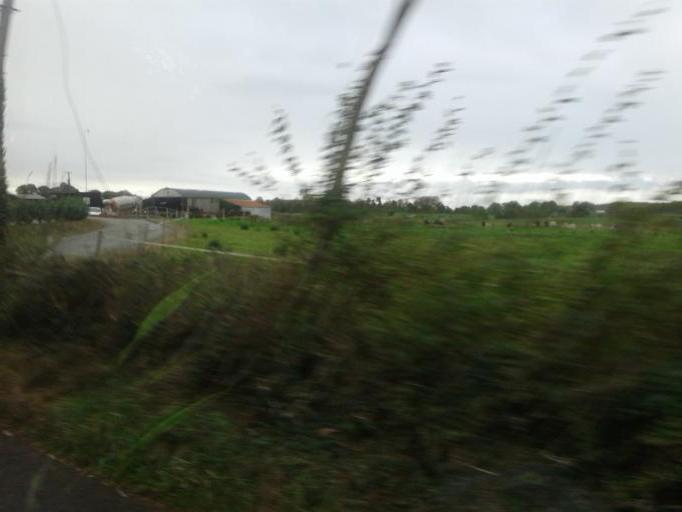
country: IE
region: Munster
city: Nenagh Bridge
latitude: 52.9315
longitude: -8.0421
